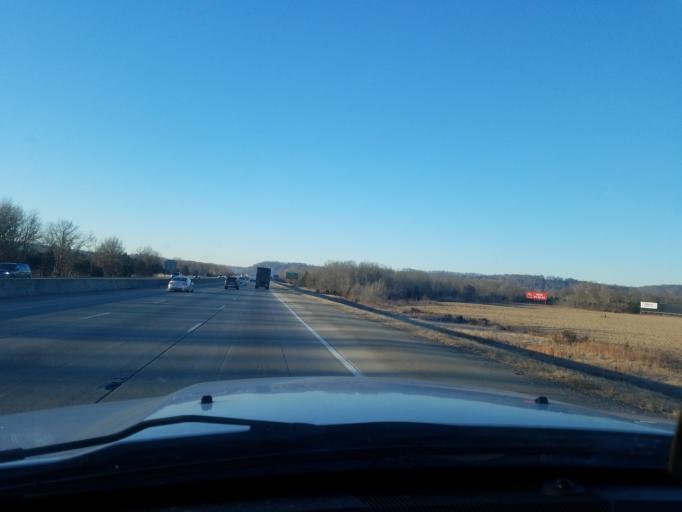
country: US
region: Kentucky
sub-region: Bullitt County
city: Lebanon Junction
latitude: 37.8195
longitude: -85.7328
